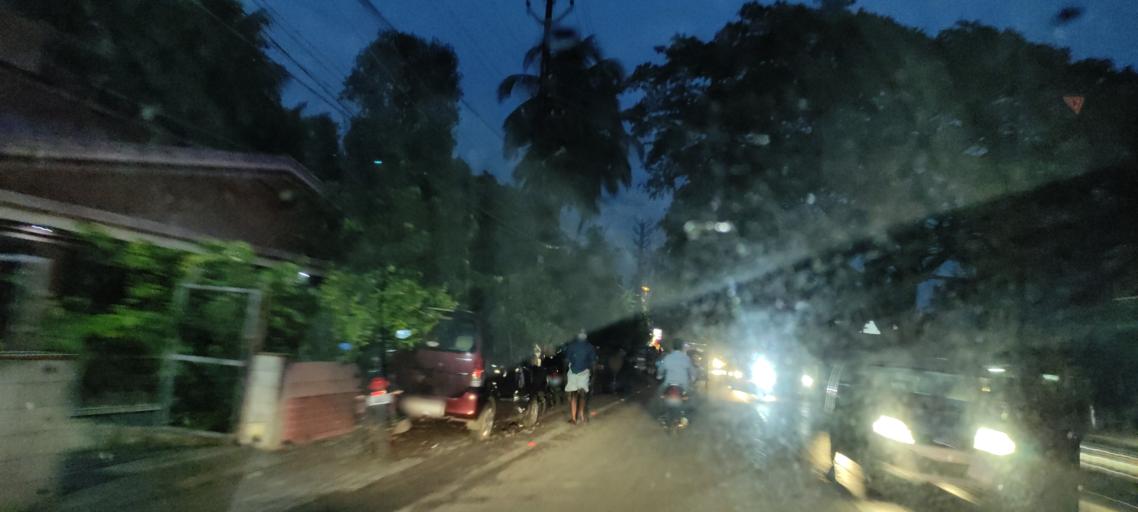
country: IN
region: Kerala
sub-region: Alappuzha
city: Arukutti
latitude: 9.8815
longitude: 76.3027
